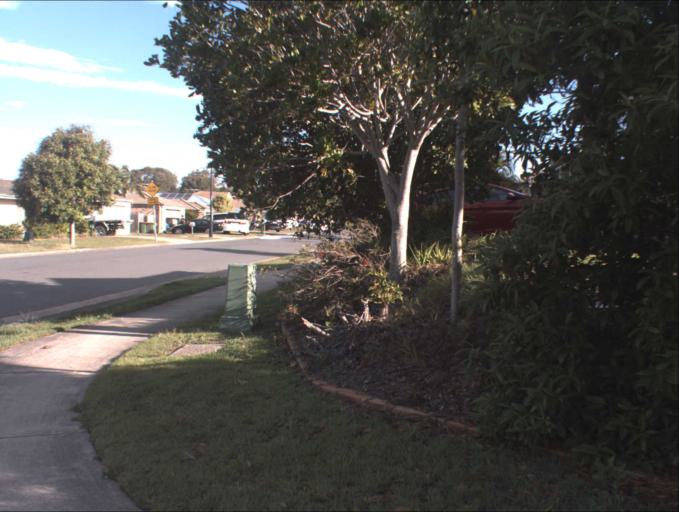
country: AU
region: Queensland
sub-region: Logan
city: Logan Reserve
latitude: -27.6975
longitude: 153.0946
